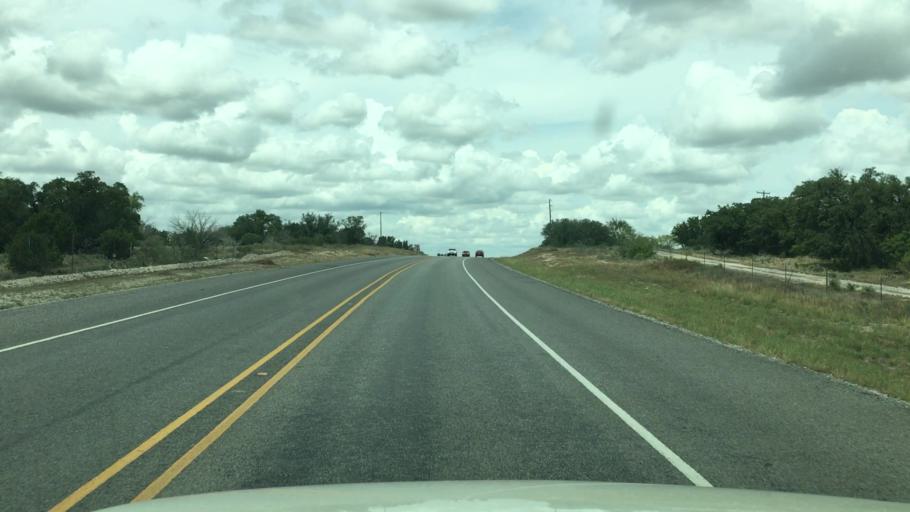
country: US
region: Texas
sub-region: McCulloch County
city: Brady
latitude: 31.0331
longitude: -99.2333
